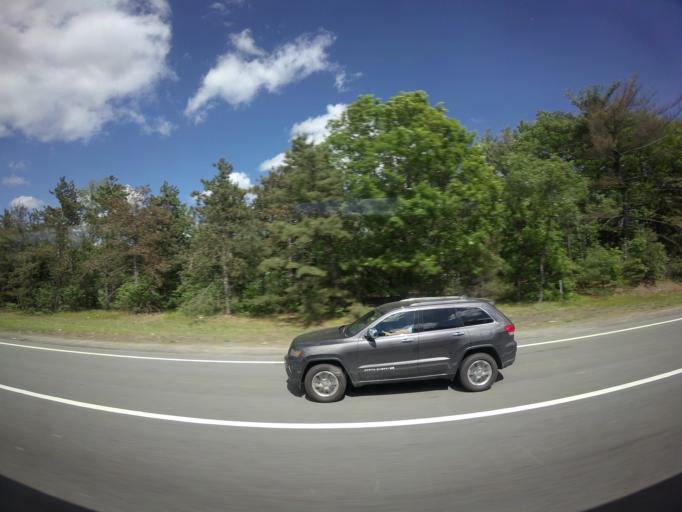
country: US
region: Massachusetts
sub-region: Middlesex County
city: Wilmington
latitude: 42.6072
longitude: -71.1725
